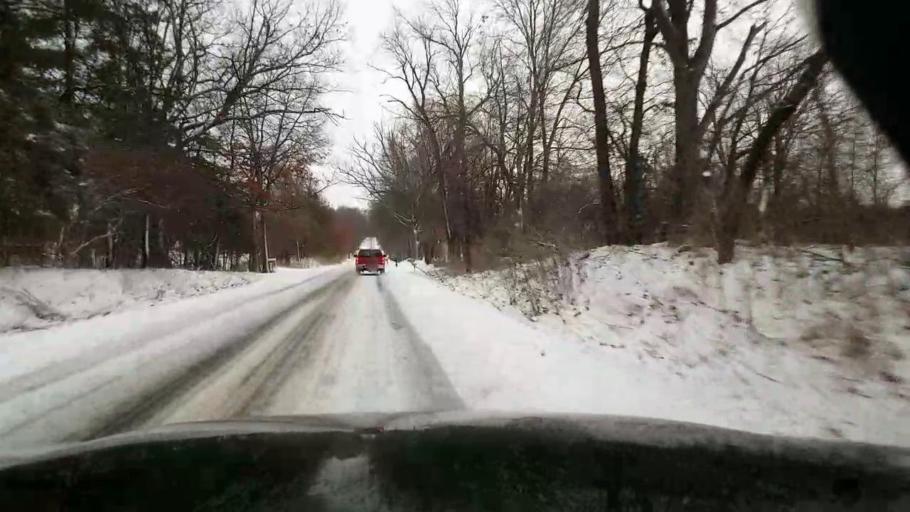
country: US
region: Michigan
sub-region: Jackson County
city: Spring Arbor
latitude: 42.1387
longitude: -84.4988
